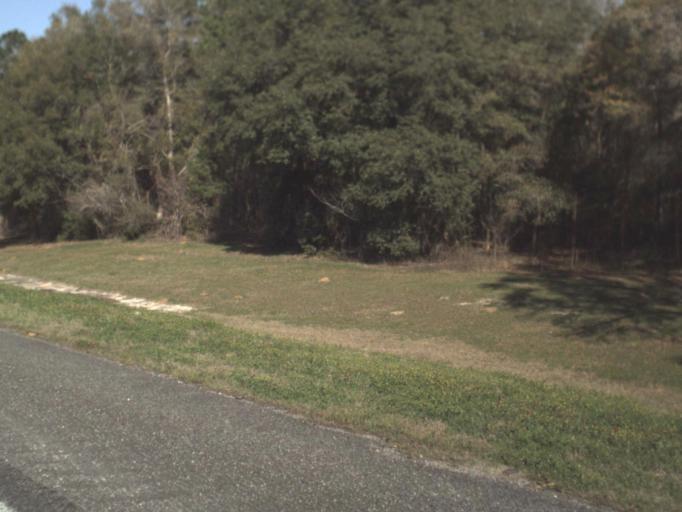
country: US
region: Florida
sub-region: Jefferson County
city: Monticello
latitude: 30.4732
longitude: -83.8553
